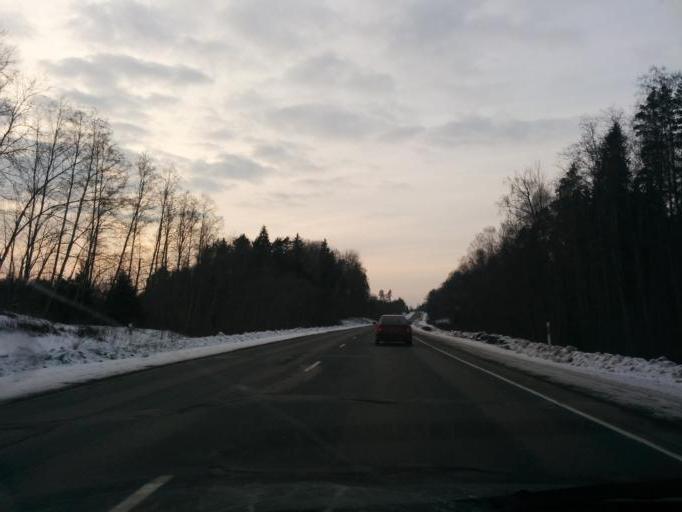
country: LV
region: Raunas
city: Rauna
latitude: 57.3158
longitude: 25.7216
